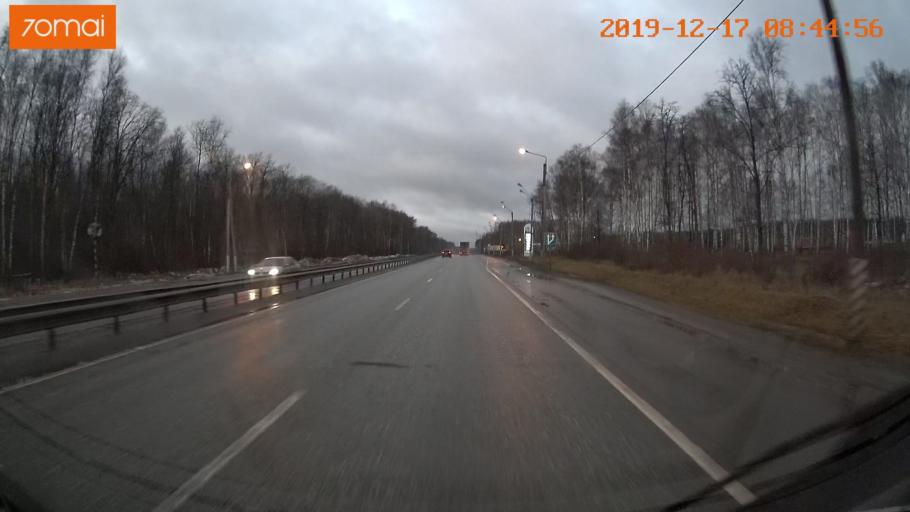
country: RU
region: Vladimir
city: Kosterevo
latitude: 55.9602
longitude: 39.6903
